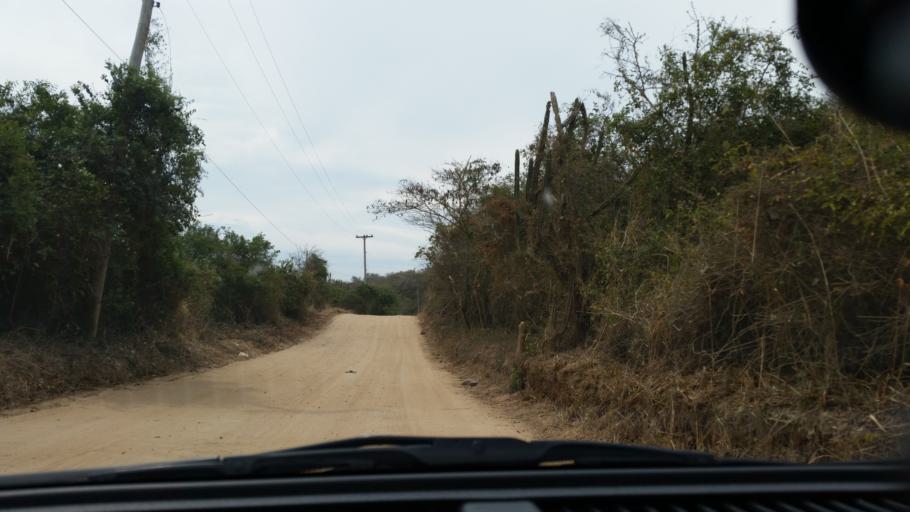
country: BR
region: Rio de Janeiro
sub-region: Cabo Frio
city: Cabo Frio
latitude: -22.8732
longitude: -41.9929
